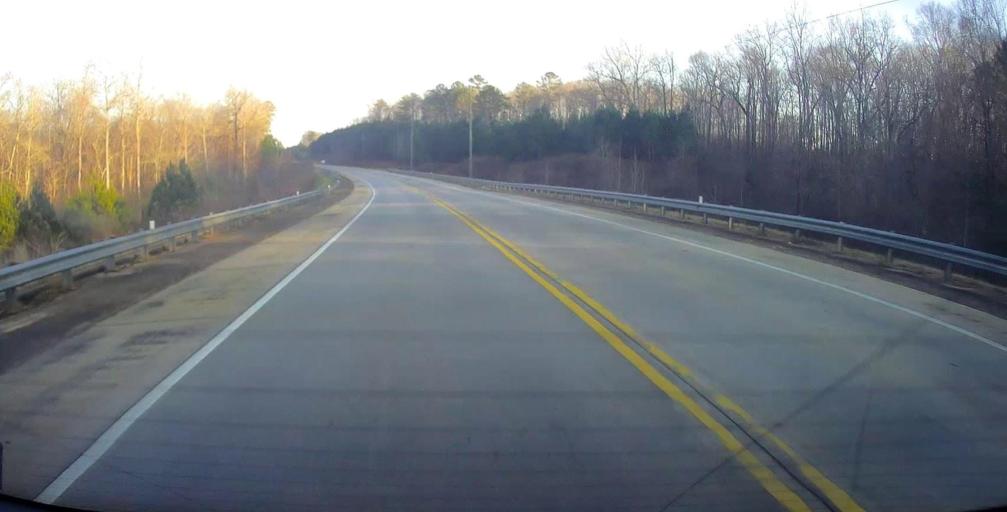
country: US
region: Georgia
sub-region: Troup County
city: La Grange
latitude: 32.9949
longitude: -85.0810
